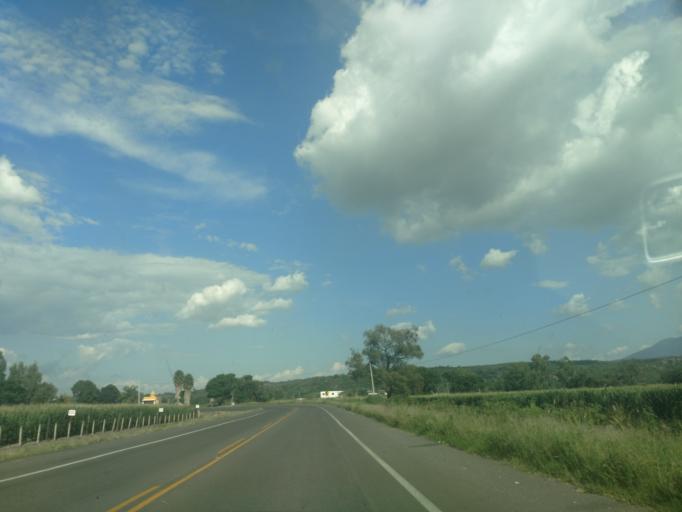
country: MX
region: Jalisco
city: Antonio Escobedo
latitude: 20.8924
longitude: -103.9950
